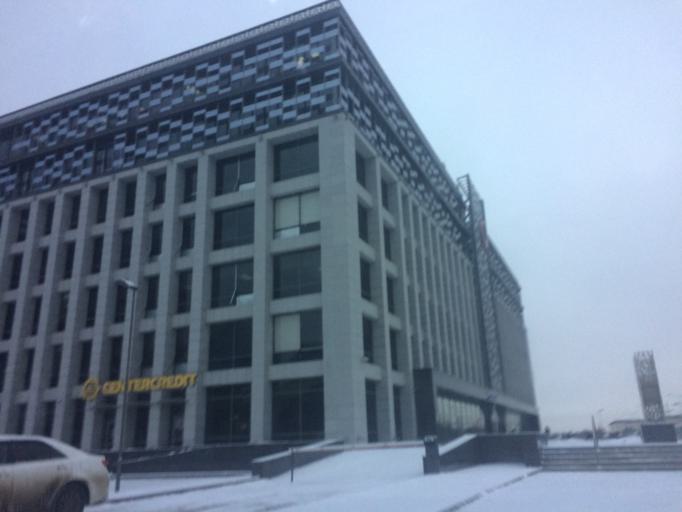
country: KZ
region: Astana Qalasy
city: Astana
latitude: 51.1362
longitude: 71.4151
